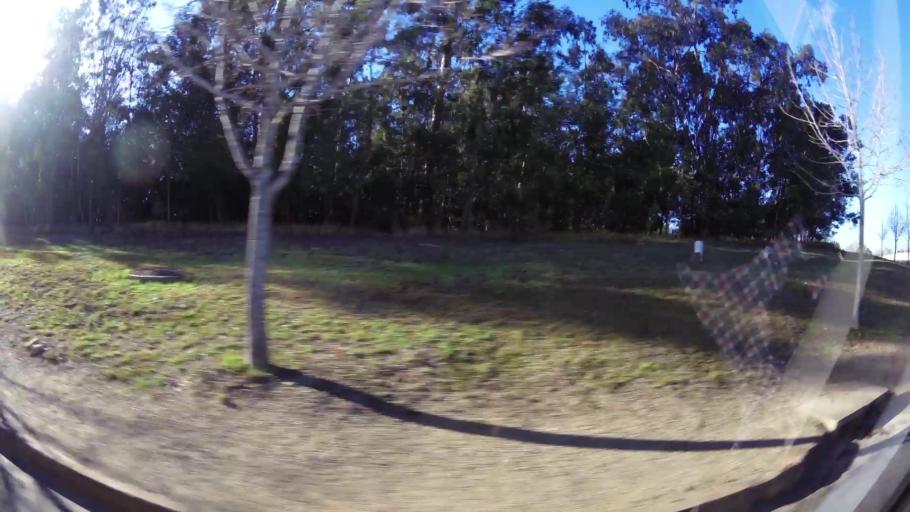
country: ZA
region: Western Cape
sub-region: Eden District Municipality
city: George
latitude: -33.9652
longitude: 22.4383
